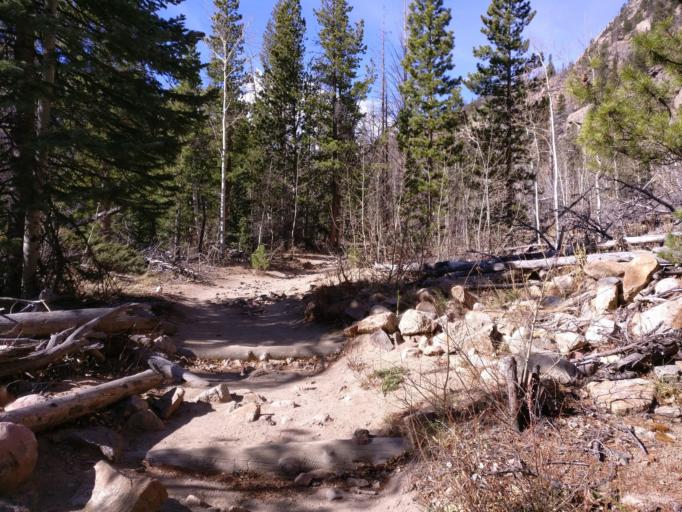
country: US
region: Colorado
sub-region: Larimer County
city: Estes Park
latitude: 40.3506
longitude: -105.6507
